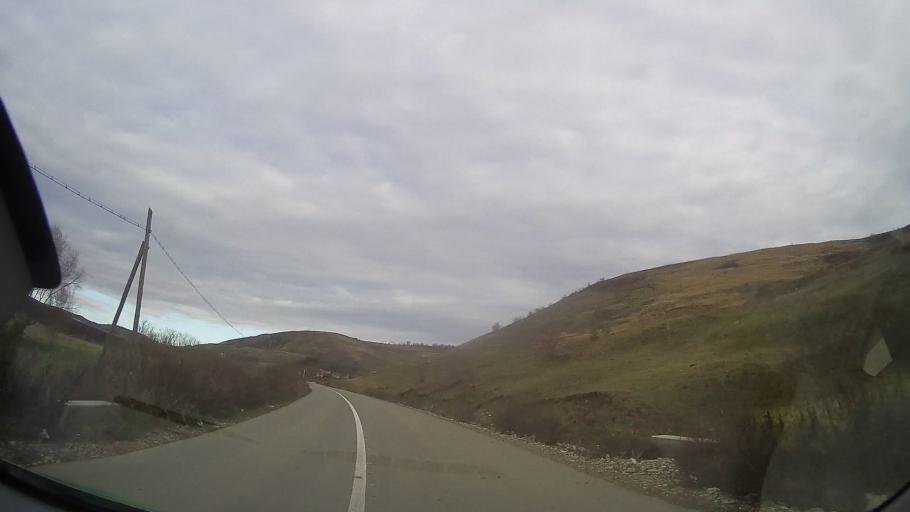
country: RO
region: Bistrita-Nasaud
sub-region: Comuna Micestii de Campie
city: Micestii de Campie
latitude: 46.8270
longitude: 24.3054
